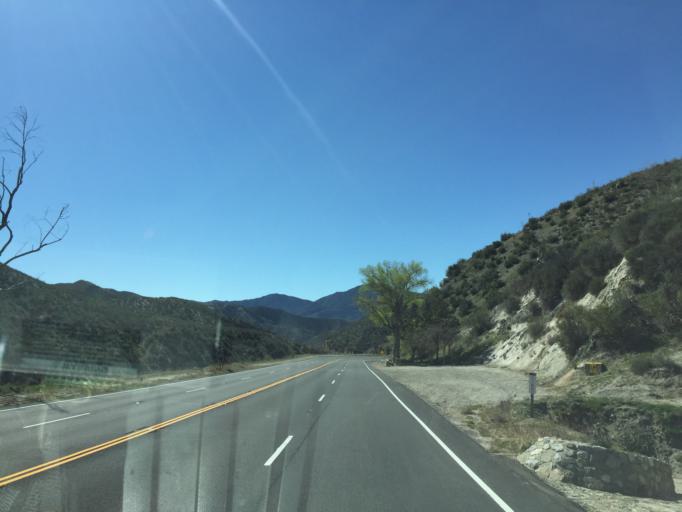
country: US
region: California
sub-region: Los Angeles County
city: Acton
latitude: 34.3566
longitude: -118.1097
